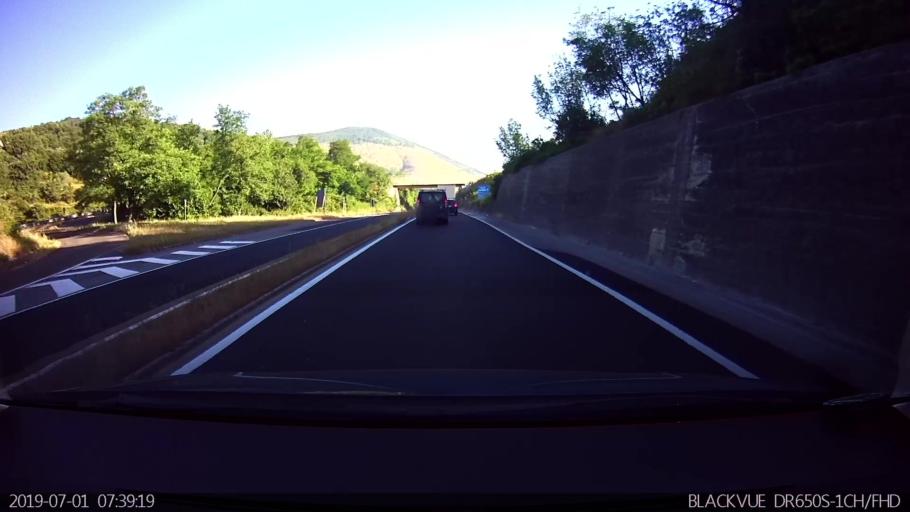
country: IT
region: Latium
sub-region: Provincia di Frosinone
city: Giuliano di Roma
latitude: 41.5486
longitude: 13.2690
